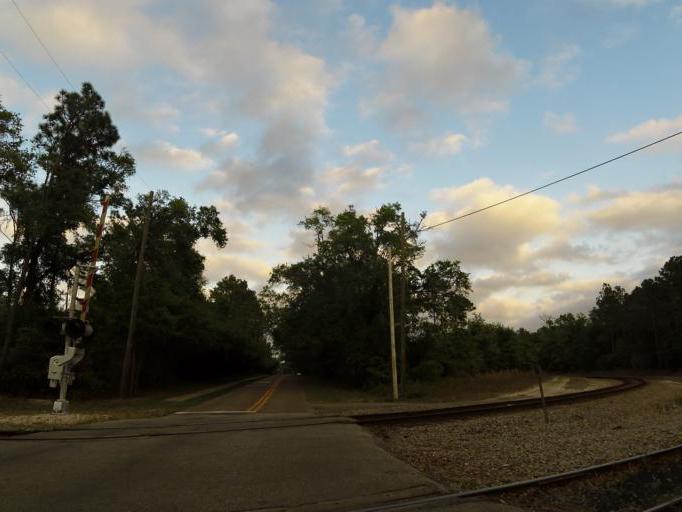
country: US
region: Florida
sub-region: Duval County
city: Jacksonville
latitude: 30.4393
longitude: -81.6103
